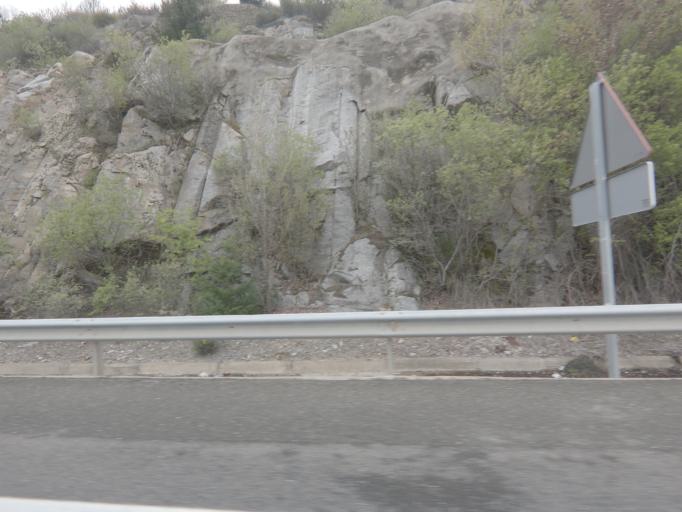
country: ES
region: Castille and Leon
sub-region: Provincia de Salamanca
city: Penacaballera
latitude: 40.3371
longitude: -5.8517
